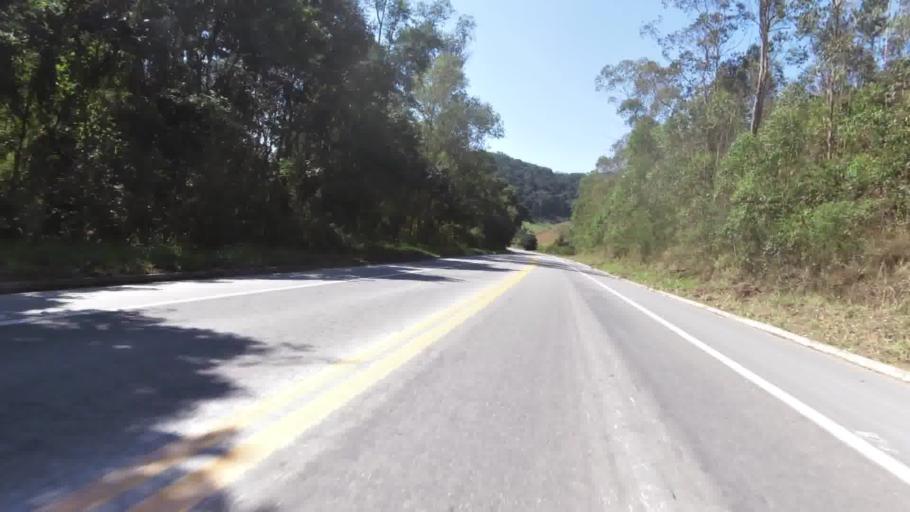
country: BR
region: Espirito Santo
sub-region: Marechal Floriano
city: Marechal Floriano
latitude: -20.4148
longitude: -40.8488
